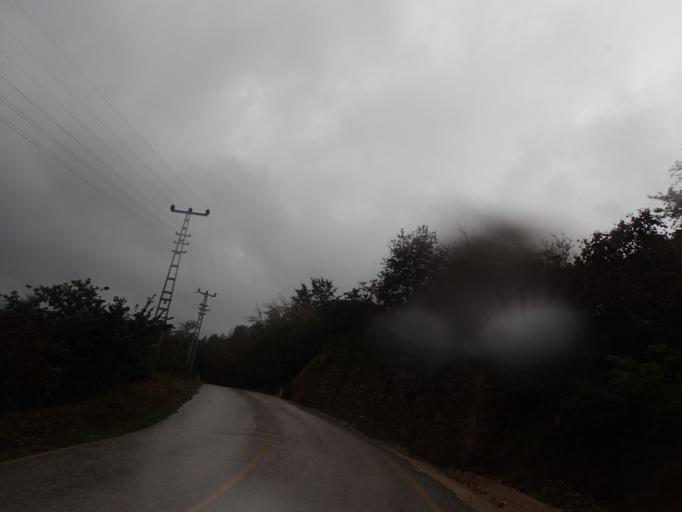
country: TR
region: Ordu
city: Persembe
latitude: 41.0440
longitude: 37.7438
